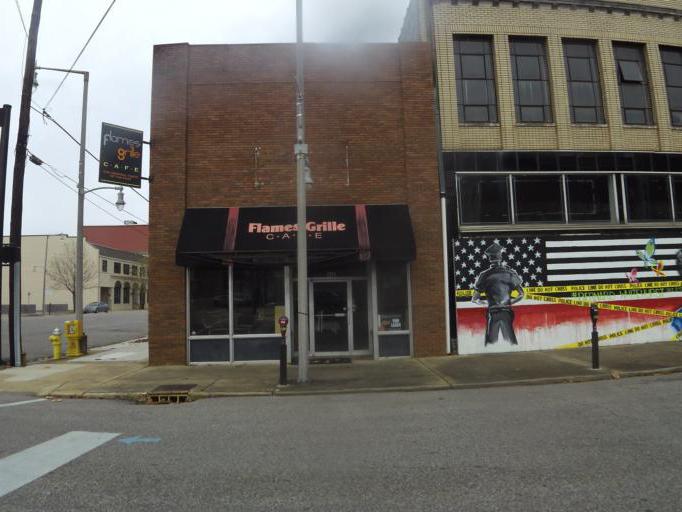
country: US
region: Alabama
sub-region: Montgomery County
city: Montgomery
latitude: 32.3771
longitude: -86.3104
